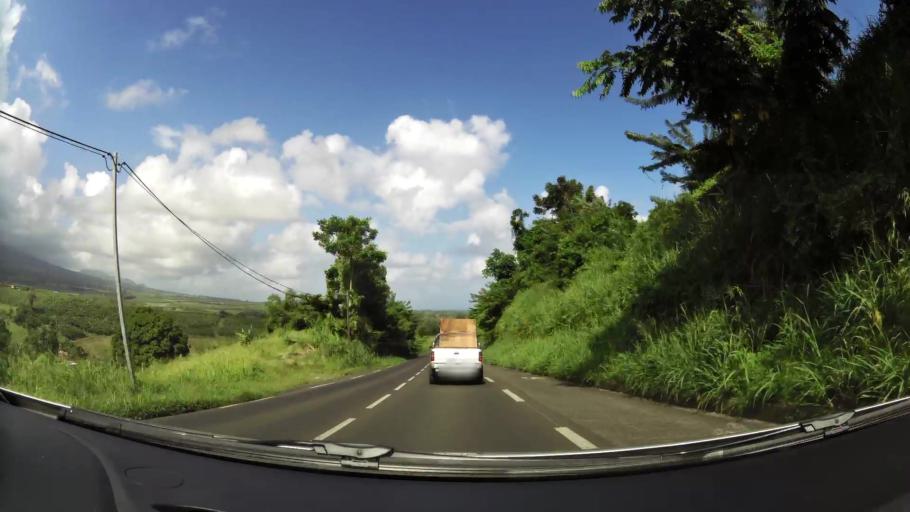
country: MQ
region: Martinique
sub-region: Martinique
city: Le Lorrain
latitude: 14.8385
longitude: -61.0784
